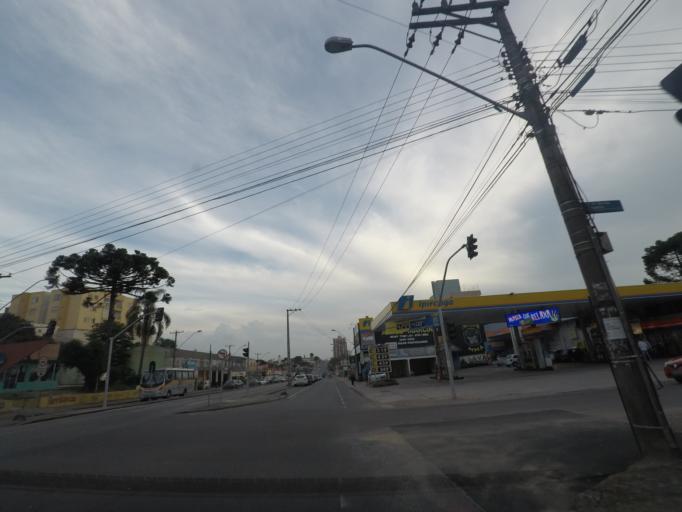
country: BR
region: Parana
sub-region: Curitiba
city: Curitiba
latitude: -25.3786
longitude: -49.2269
